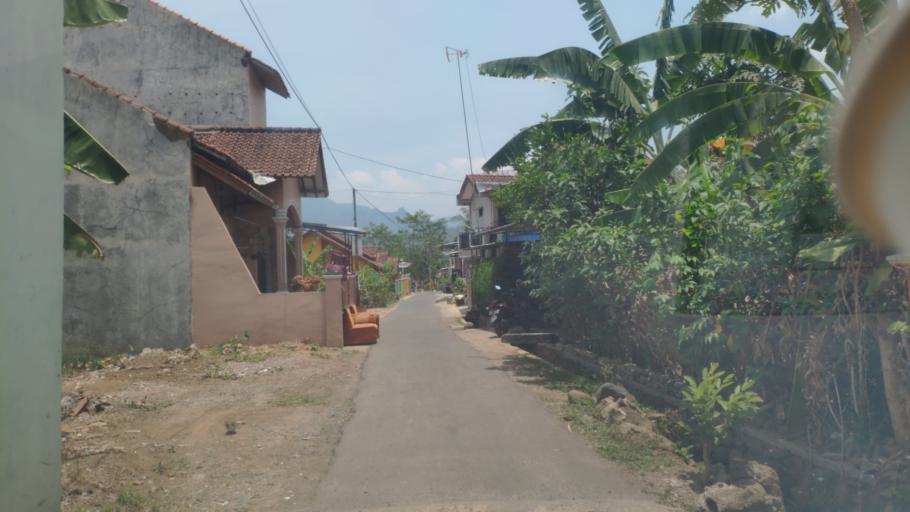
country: ID
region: Central Java
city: Wonosobo
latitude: -7.3899
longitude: 109.7070
